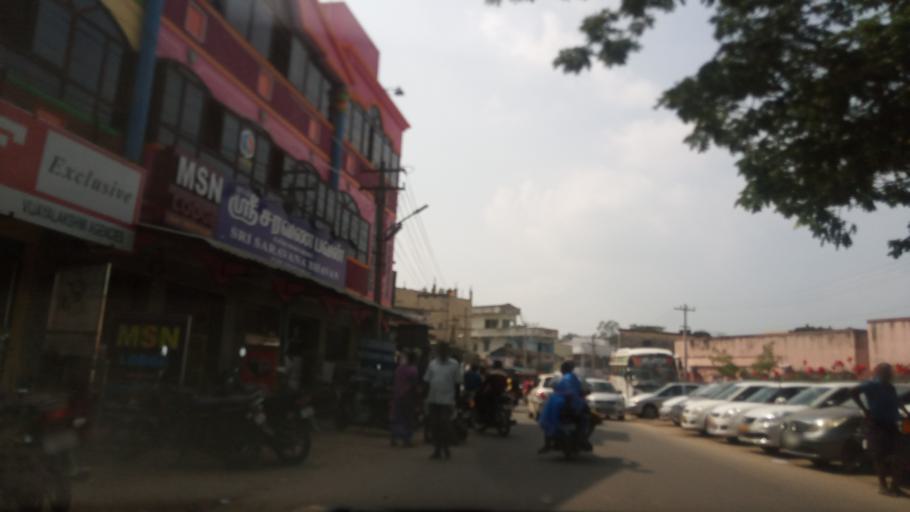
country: IN
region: Tamil Nadu
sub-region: Vellore
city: Arakkonam
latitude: 13.0847
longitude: 79.6659
